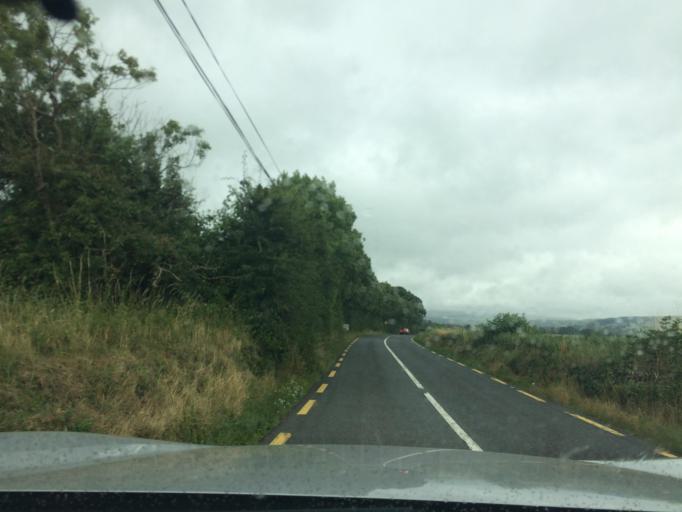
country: IE
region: Munster
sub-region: South Tipperary
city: Cluain Meala
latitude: 52.2938
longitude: -7.7776
